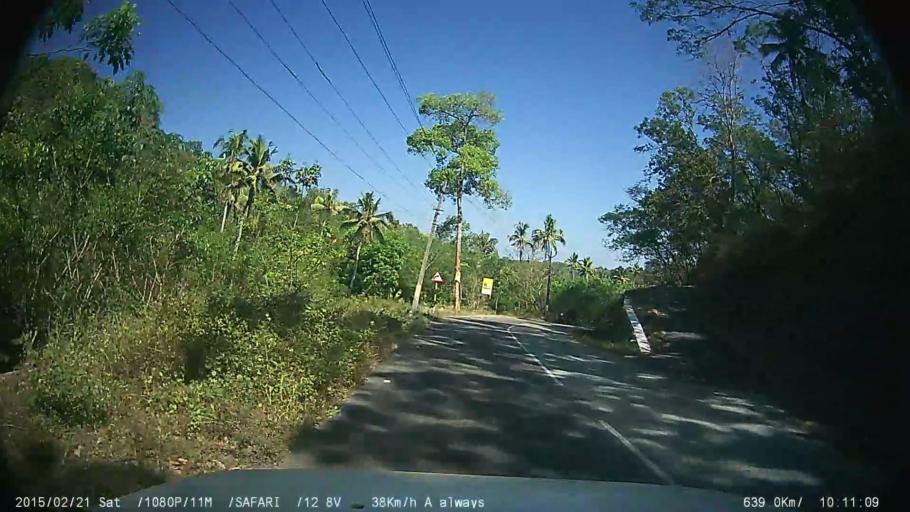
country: IN
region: Kerala
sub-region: Ernakulam
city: Muvattupuzha
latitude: 9.8824
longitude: 76.6199
